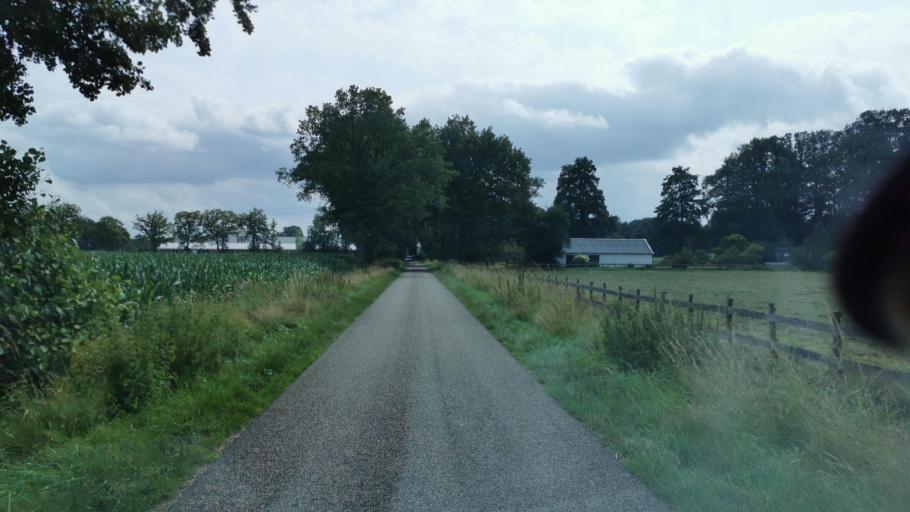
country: NL
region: Overijssel
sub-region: Gemeente Losser
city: Losser
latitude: 52.2441
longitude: 6.9961
